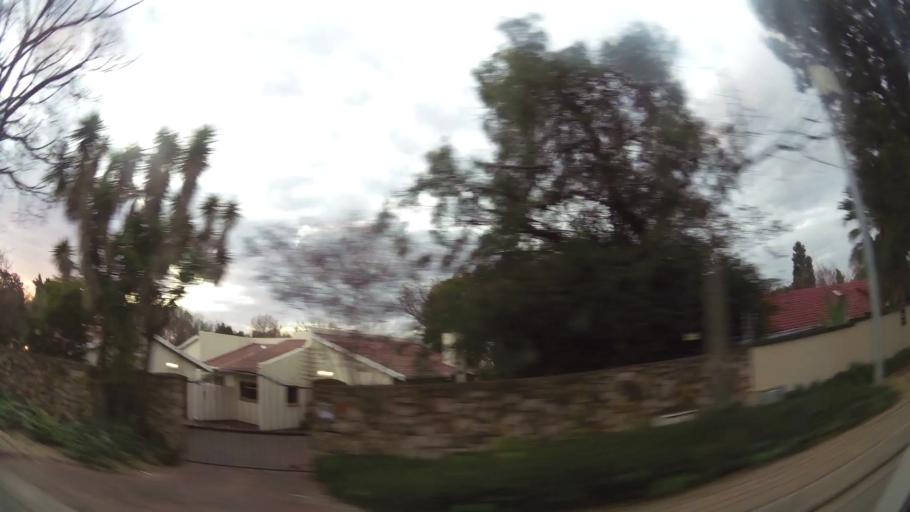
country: ZA
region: Gauteng
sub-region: City of Johannesburg Metropolitan Municipality
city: Diepsloot
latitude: -26.0379
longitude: 28.0046
